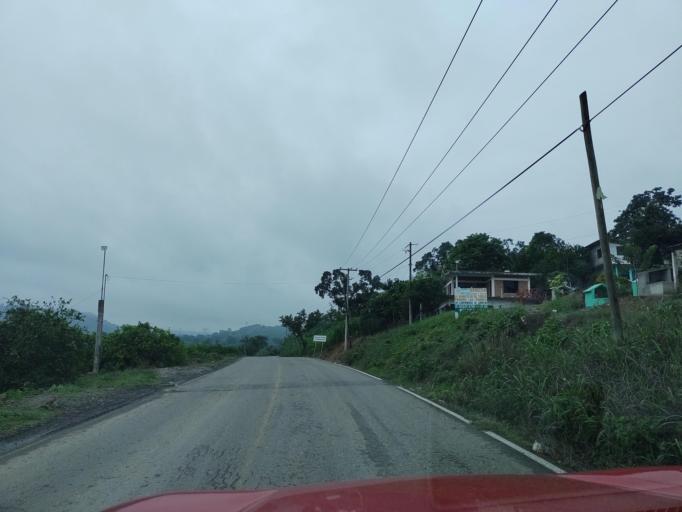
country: MX
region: Puebla
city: Espinal
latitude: 20.2626
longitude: -97.3640
